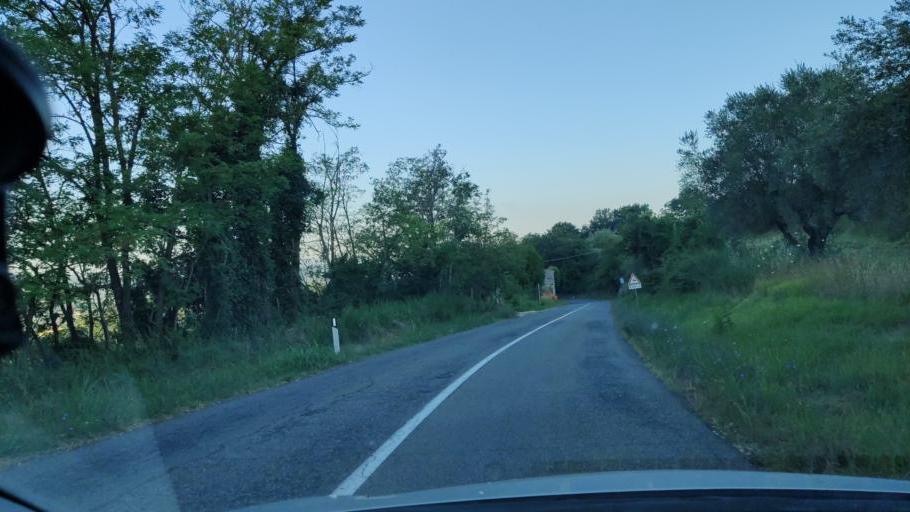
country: IT
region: Umbria
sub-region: Provincia di Terni
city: Giove
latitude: 42.5017
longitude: 12.3225
